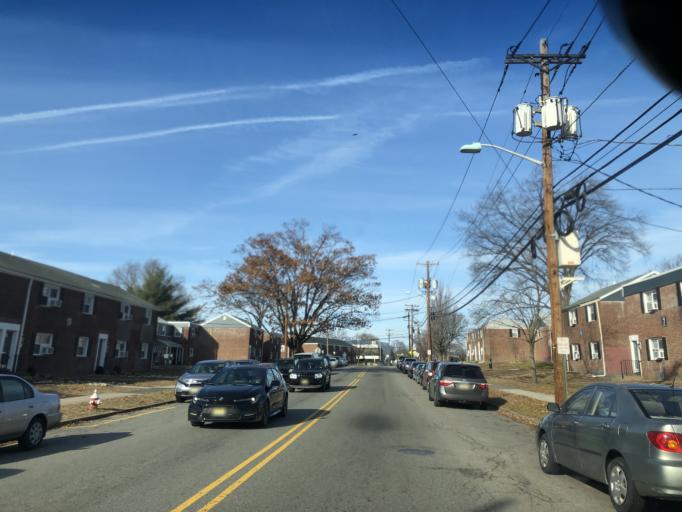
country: US
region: New Jersey
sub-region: Bergen County
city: Elmwood Park
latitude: 40.9168
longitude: -74.1239
